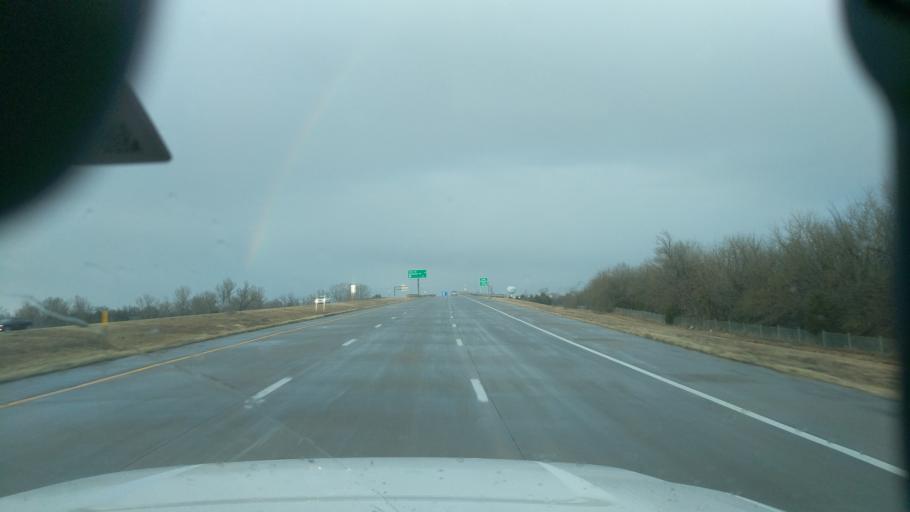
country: US
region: Kansas
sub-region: Harvey County
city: Newton
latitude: 38.0317
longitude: -97.3264
